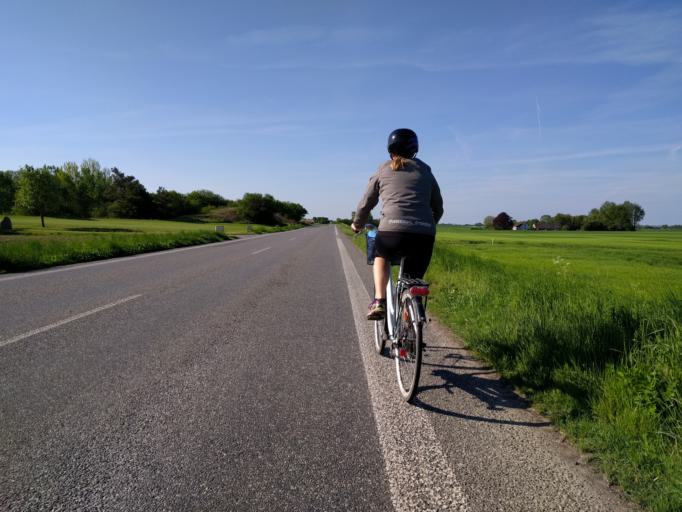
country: DK
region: Zealand
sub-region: Guldborgsund Kommune
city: Stubbekobing
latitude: 54.8193
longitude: 11.9939
